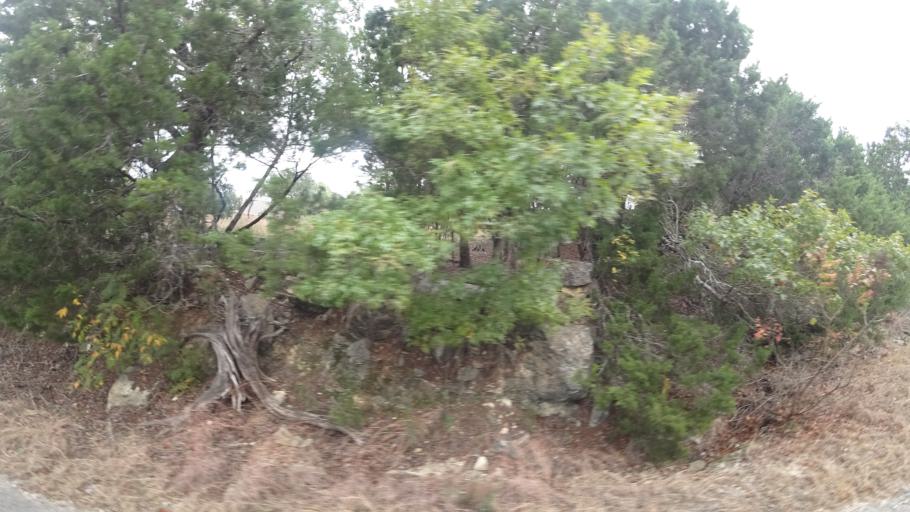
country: US
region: Texas
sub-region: Travis County
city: Hudson Bend
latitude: 30.3720
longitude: -97.9213
